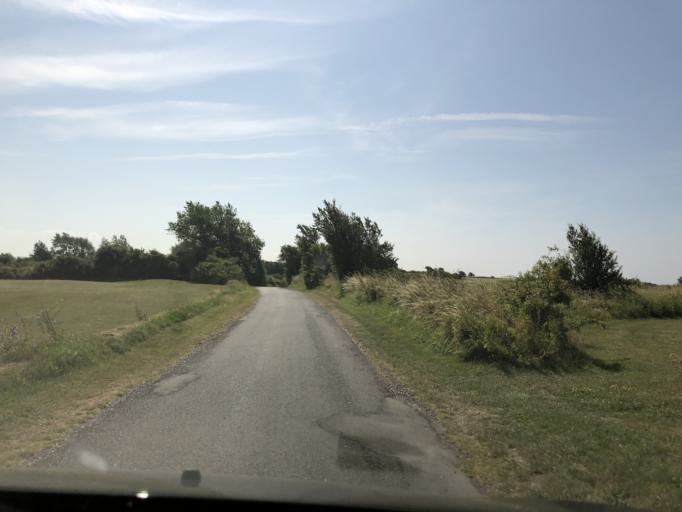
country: DK
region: South Denmark
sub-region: Faaborg-Midtfyn Kommune
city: Faaborg
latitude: 54.9669
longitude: 10.2097
